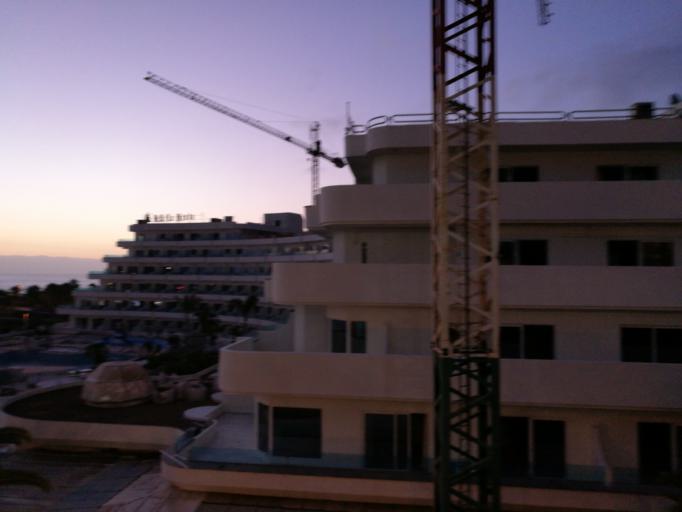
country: ES
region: Canary Islands
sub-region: Provincia de Santa Cruz de Tenerife
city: Playa de las Americas
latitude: 28.0800
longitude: -16.7340
